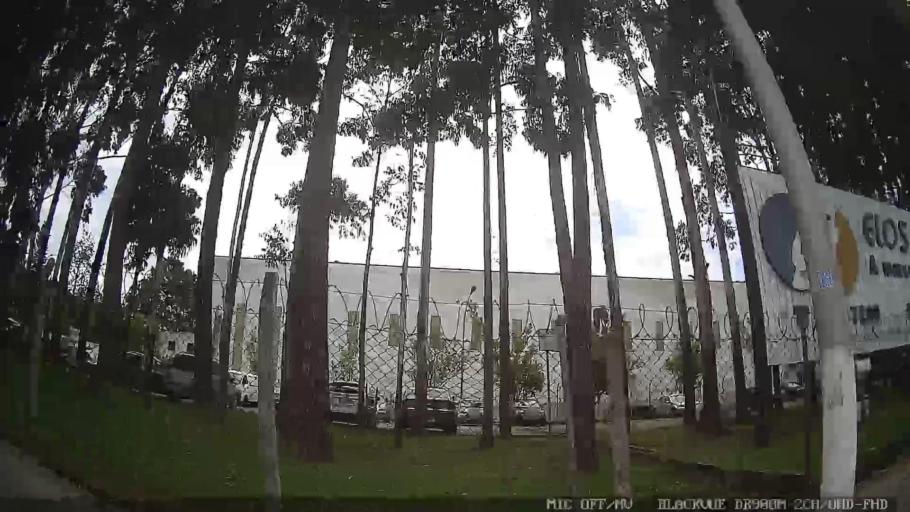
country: BR
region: Sao Paulo
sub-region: Aruja
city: Aruja
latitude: -23.4224
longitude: -46.3750
